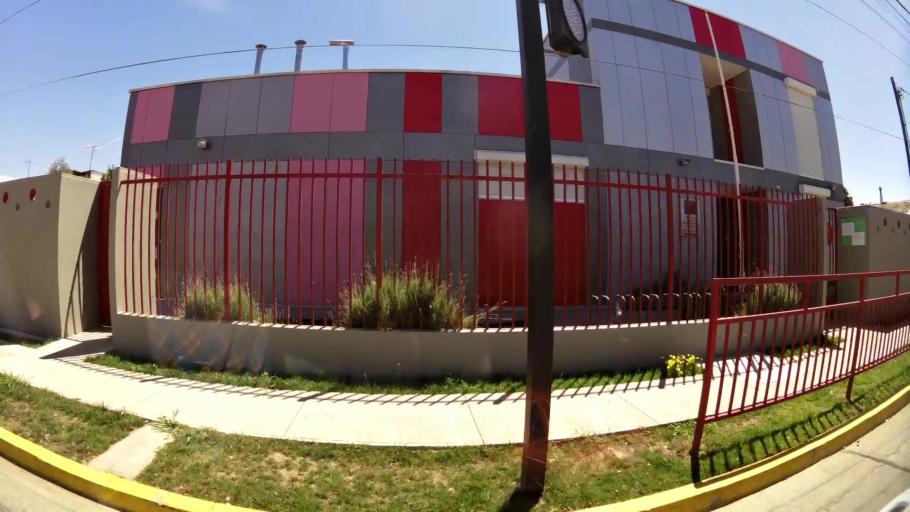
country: CL
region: O'Higgins
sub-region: Provincia de Cachapoal
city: Rancagua
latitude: -34.1604
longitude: -70.7522
